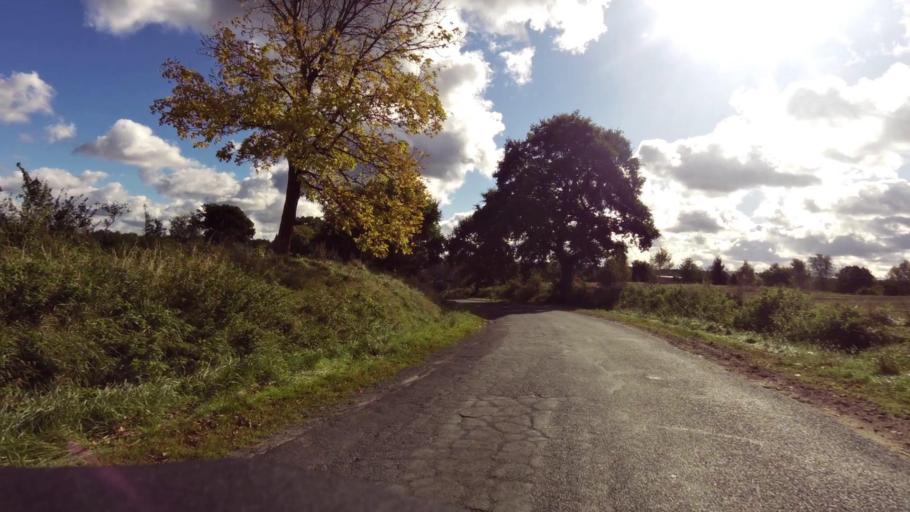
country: PL
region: West Pomeranian Voivodeship
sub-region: Powiat bialogardzki
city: Bialogard
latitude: 53.9932
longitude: 16.0651
